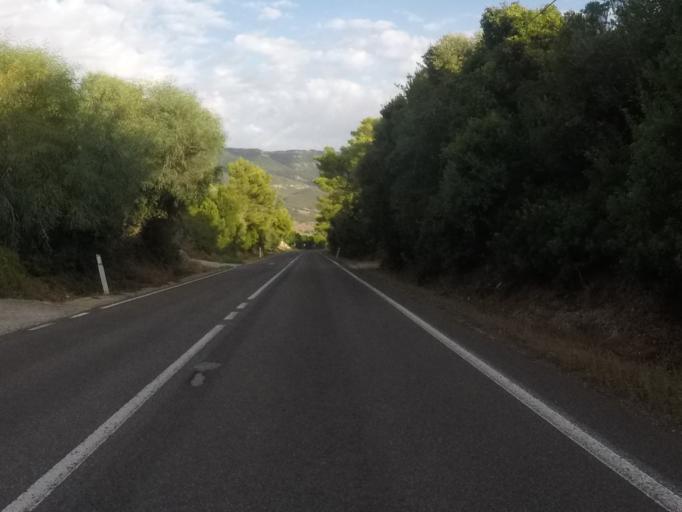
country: IT
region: Sardinia
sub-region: Provincia di Sassari
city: Alghero
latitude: 40.5124
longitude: 8.3537
